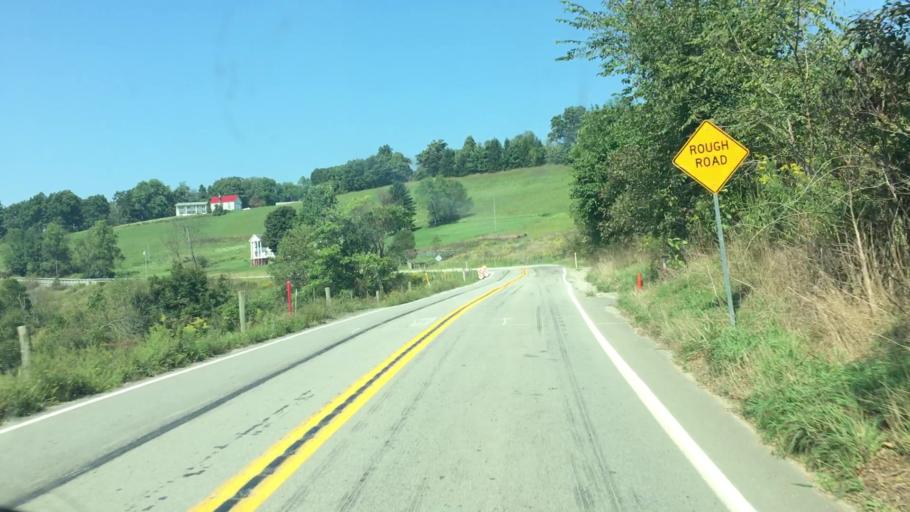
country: US
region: Pennsylvania
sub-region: Greene County
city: Waynesburg
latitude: 39.9834
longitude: -80.3417
